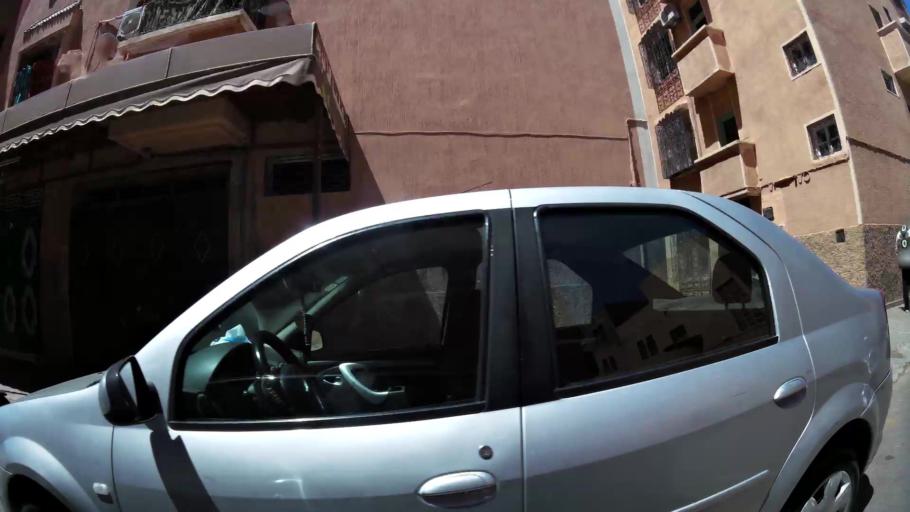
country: MA
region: Marrakech-Tensift-Al Haouz
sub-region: Marrakech
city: Marrakesh
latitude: 31.6285
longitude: -8.0526
